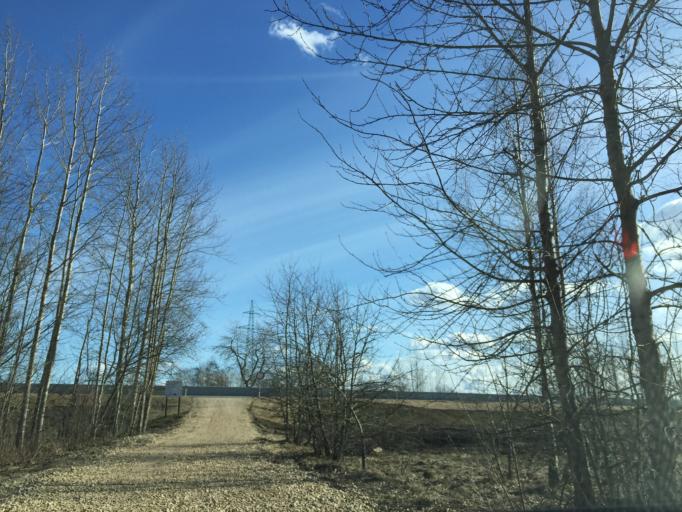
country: LV
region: Ogre
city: Ogre
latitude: 56.8106
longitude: 24.5954
